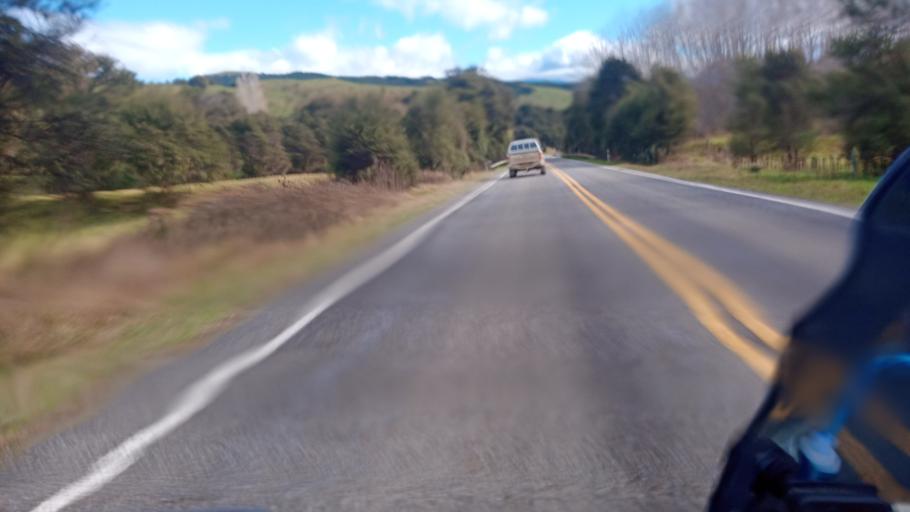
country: NZ
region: Gisborne
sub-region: Gisborne District
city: Gisborne
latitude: -37.9754
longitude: 178.2582
